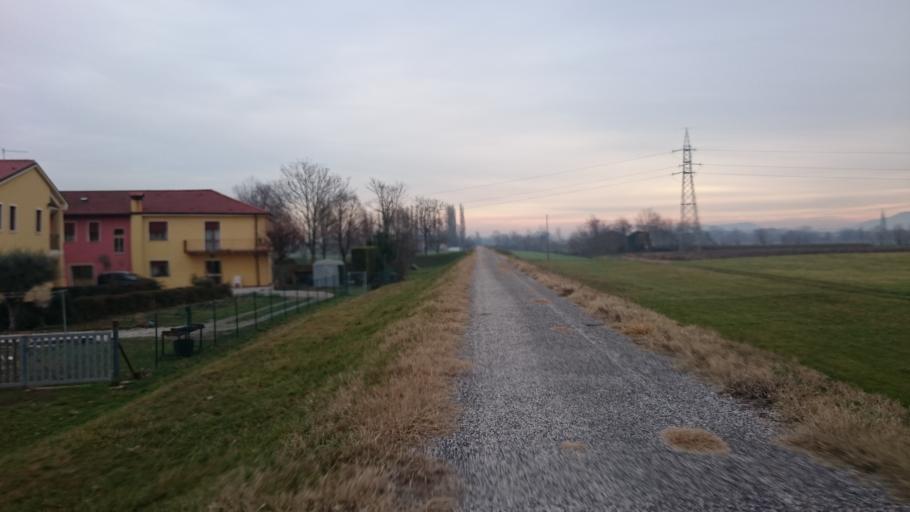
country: IT
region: Veneto
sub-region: Provincia di Padova
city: Cervarese Santa Croce
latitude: 45.4357
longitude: 11.6829
